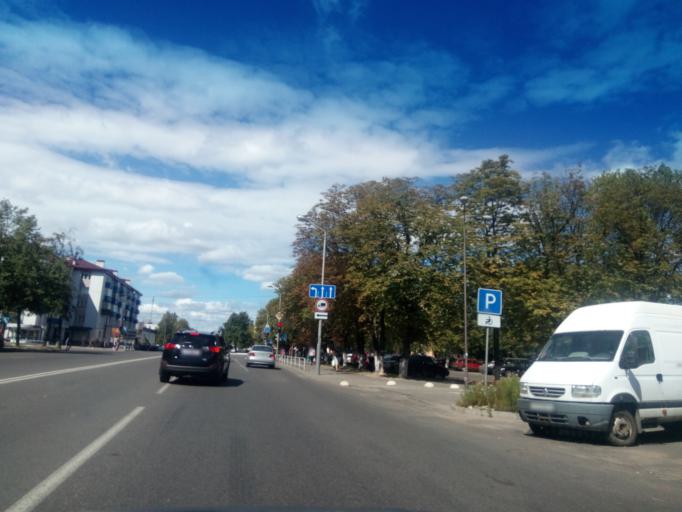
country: BY
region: Vitebsk
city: Polatsk
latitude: 55.4905
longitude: 28.7815
